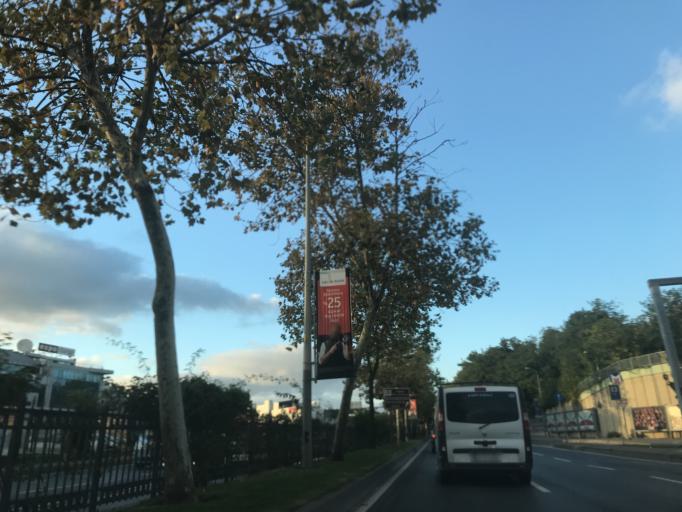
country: TR
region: Istanbul
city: Sisli
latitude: 41.1162
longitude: 29.0245
